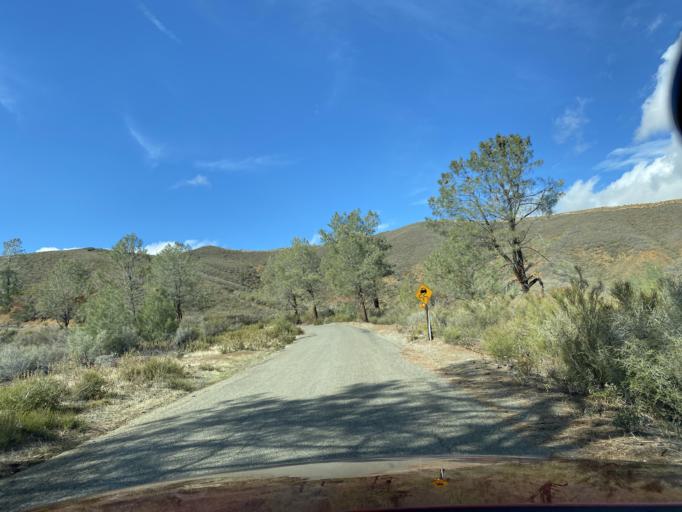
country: US
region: California
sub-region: Lake County
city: Lucerne
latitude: 39.3656
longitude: -122.6234
